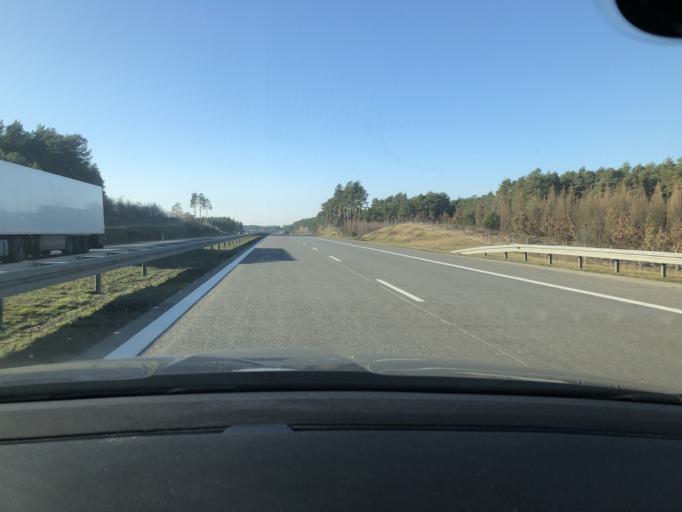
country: PL
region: Lubusz
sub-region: Powiat sulecinski
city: Torzym
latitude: 52.3290
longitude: 15.0395
